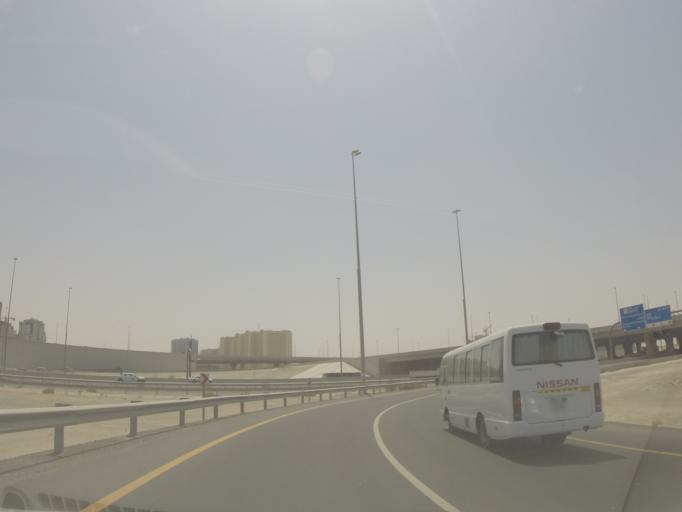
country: AE
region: Dubai
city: Dubai
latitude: 25.0438
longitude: 55.1992
